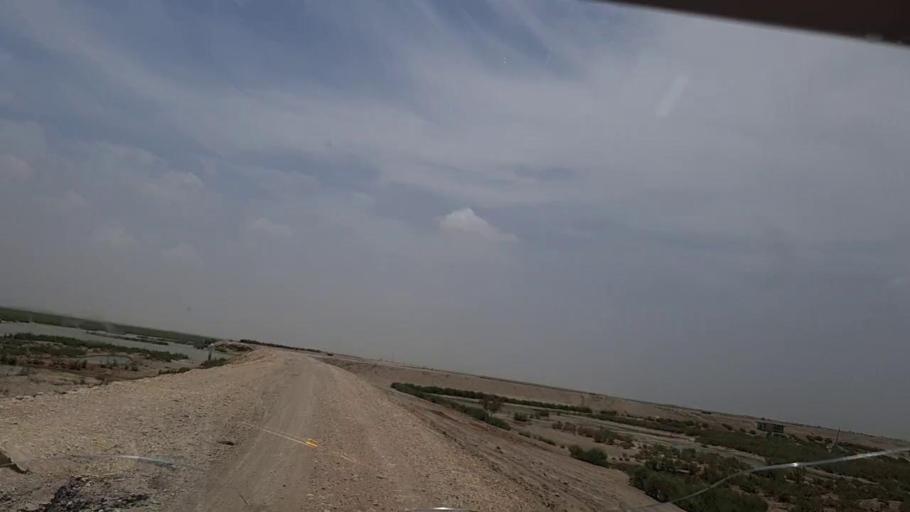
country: PK
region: Sindh
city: Bhan
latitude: 26.5086
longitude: 67.6277
